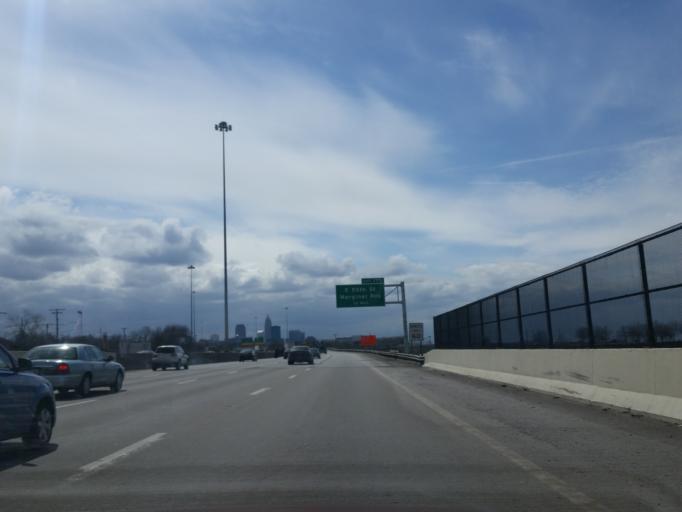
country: US
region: Ohio
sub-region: Cuyahoga County
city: Bratenahl
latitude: 41.5362
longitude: -81.6436
